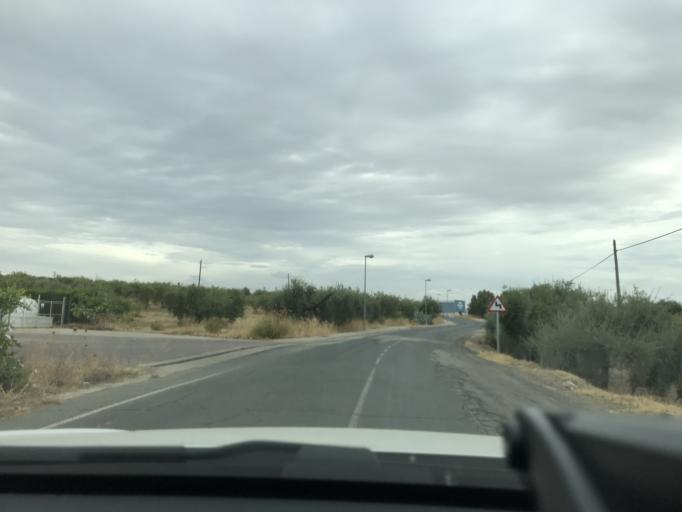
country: ES
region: Andalusia
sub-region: Provincia de Sevilla
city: Villanueva del Rio y Minas
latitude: 37.6476
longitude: -5.7102
